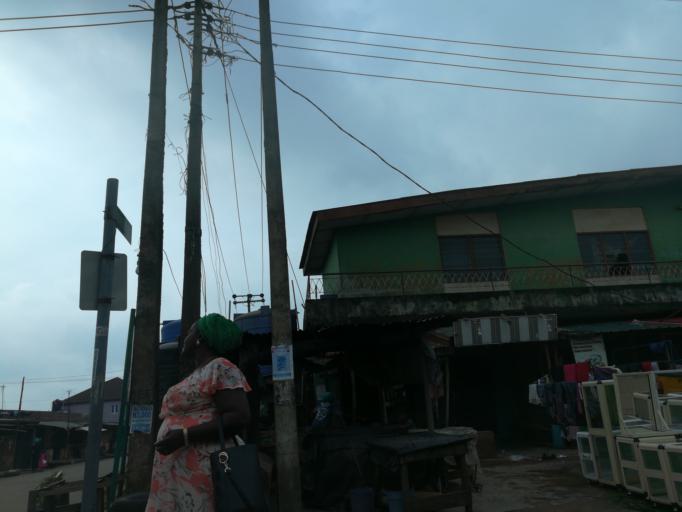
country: NG
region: Lagos
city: Agege
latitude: 6.6085
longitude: 3.3156
